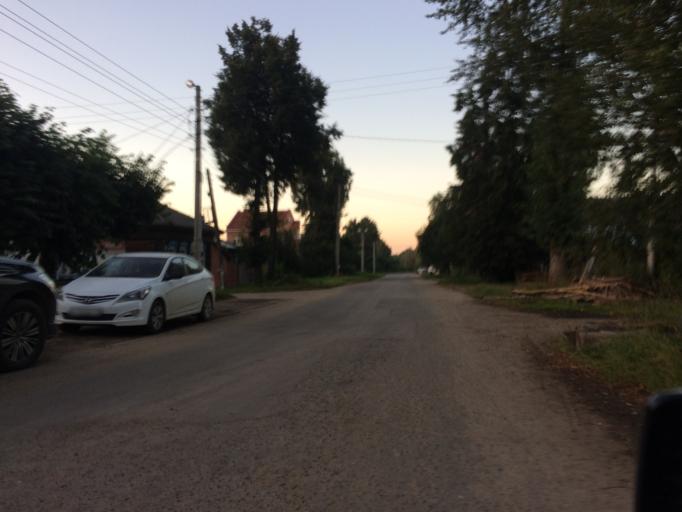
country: RU
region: Mariy-El
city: Yoshkar-Ola
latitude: 56.6401
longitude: 47.9096
